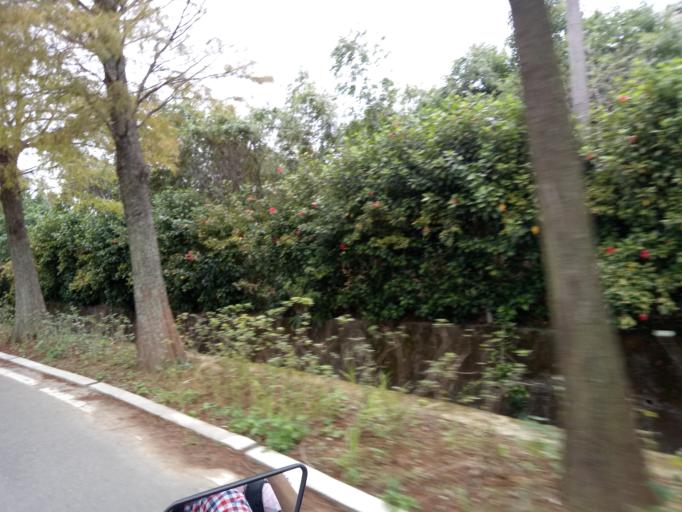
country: TW
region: Taiwan
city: Daxi
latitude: 24.8741
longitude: 121.2557
